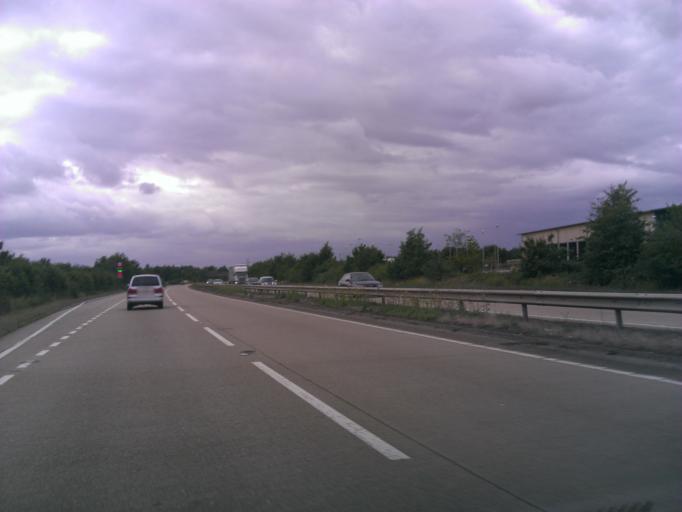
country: GB
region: England
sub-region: Essex
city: Wivenhoe
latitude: 51.9009
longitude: 0.9795
